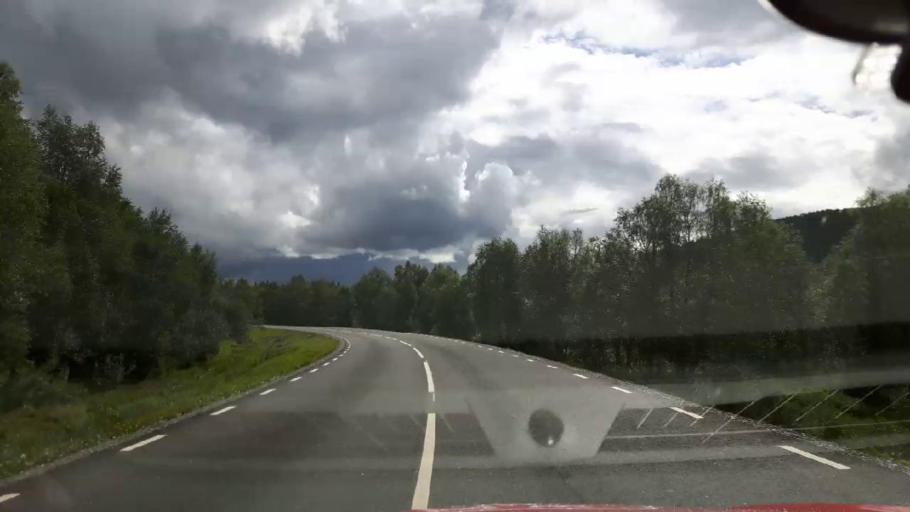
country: NO
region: Nord-Trondelag
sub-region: Royrvik
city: Royrvik
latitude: 64.8883
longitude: 14.1915
